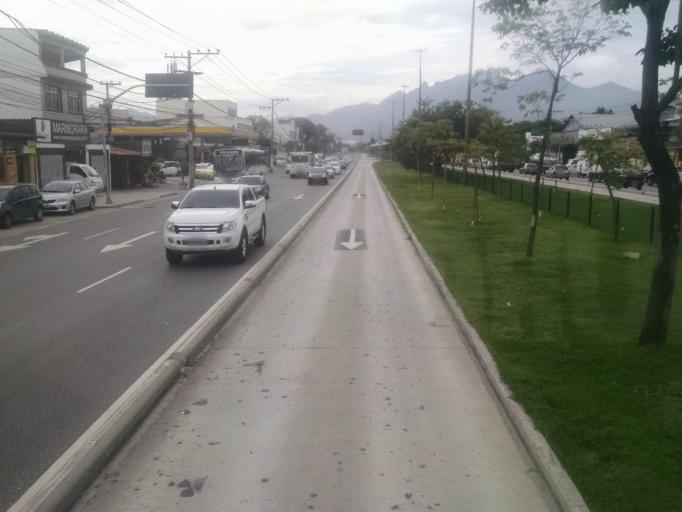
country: BR
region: Rio de Janeiro
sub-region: Nilopolis
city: Nilopolis
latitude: -22.9592
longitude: -43.3857
